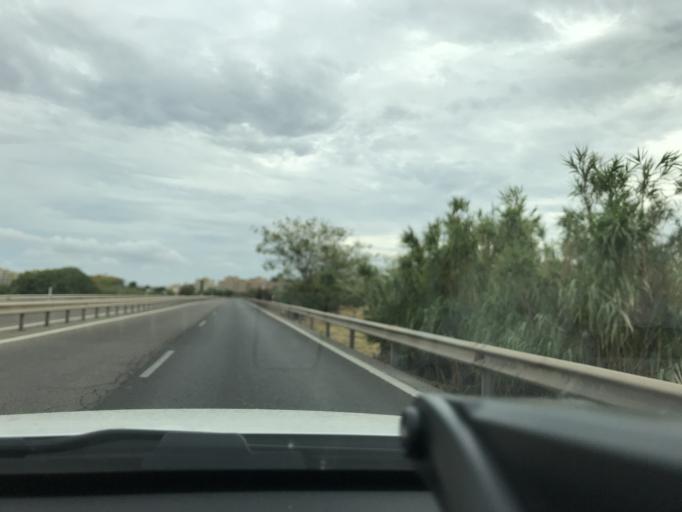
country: ES
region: Andalusia
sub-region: Provincia de Sevilla
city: Sevilla
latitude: 37.4316
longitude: -5.9654
